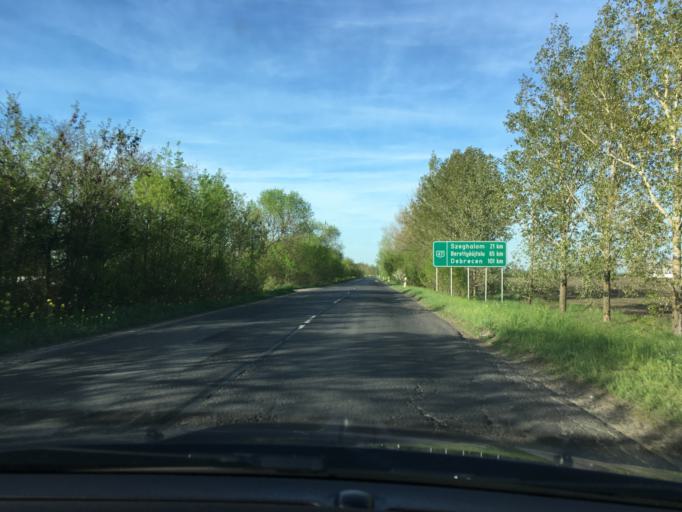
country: HU
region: Bekes
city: Korostarcsa
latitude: 46.8916
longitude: 21.0413
